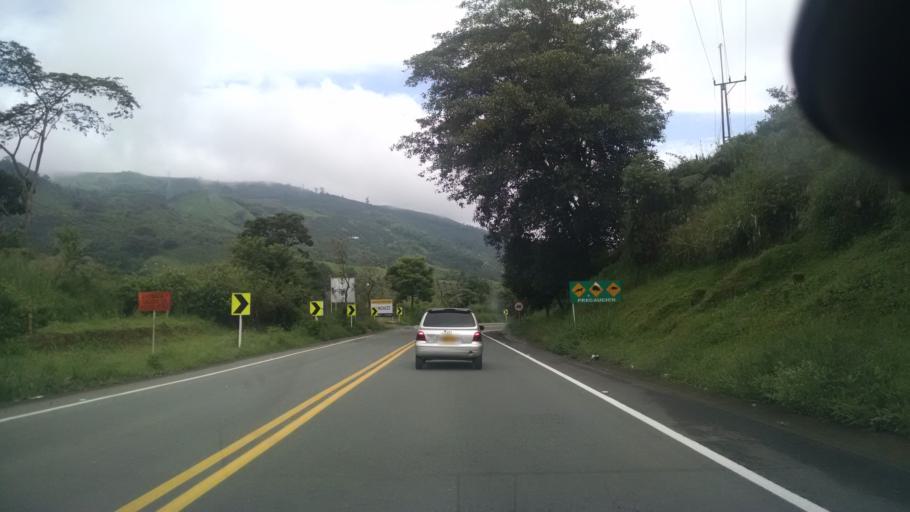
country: CO
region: Caldas
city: Palestina
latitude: 5.0287
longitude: -75.5983
